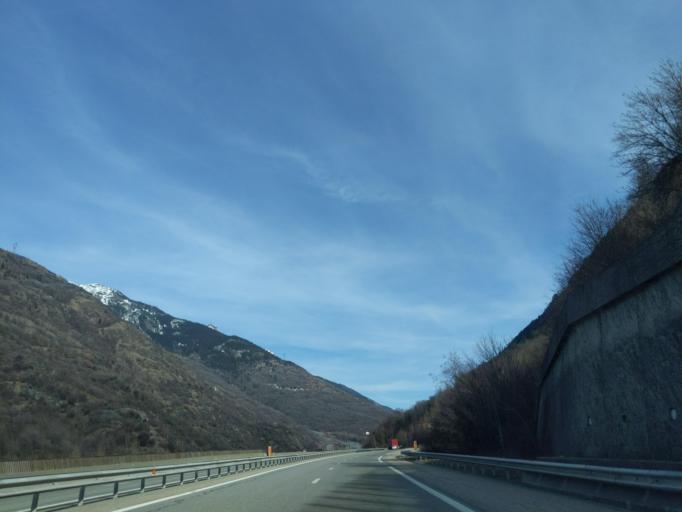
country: FR
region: Rhone-Alpes
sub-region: Departement de la Savoie
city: Saint-Michel-de-Maurienne
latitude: 45.2095
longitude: 6.4849
